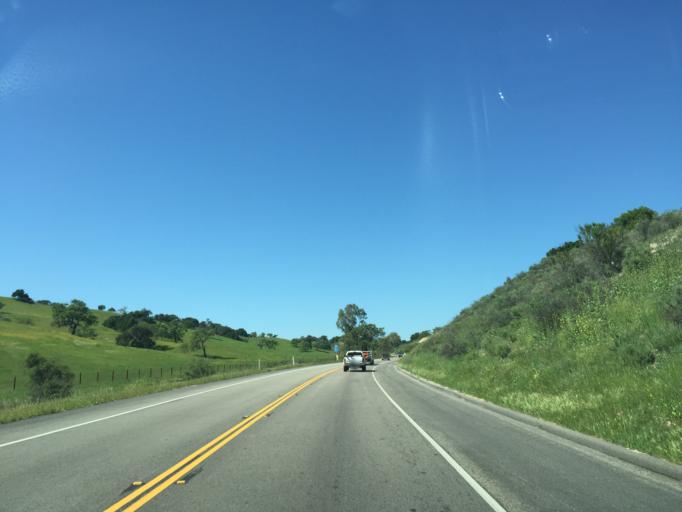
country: US
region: California
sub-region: Santa Barbara County
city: Los Olivos
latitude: 34.6707
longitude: -120.1272
